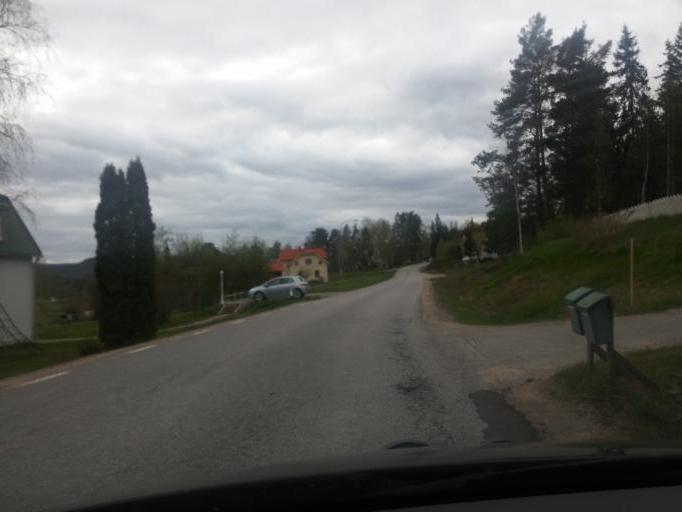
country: SE
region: Gaevleborg
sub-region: Ljusdals Kommun
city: Ljusdal
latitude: 61.8584
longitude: 16.0283
